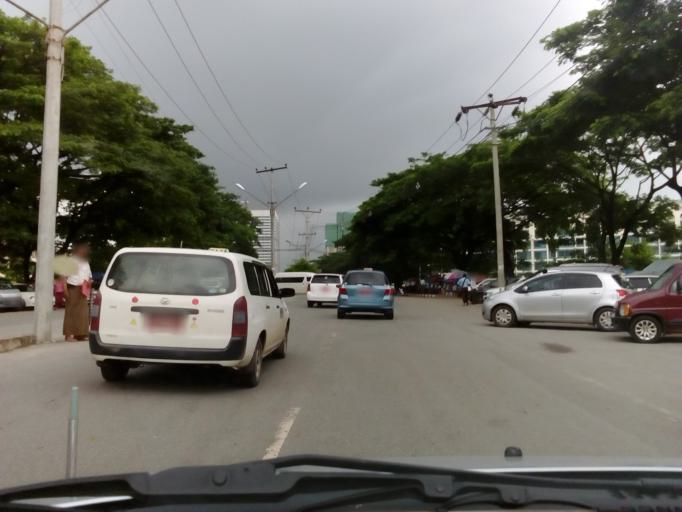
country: MM
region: Yangon
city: Yangon
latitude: 16.8235
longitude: 96.1618
